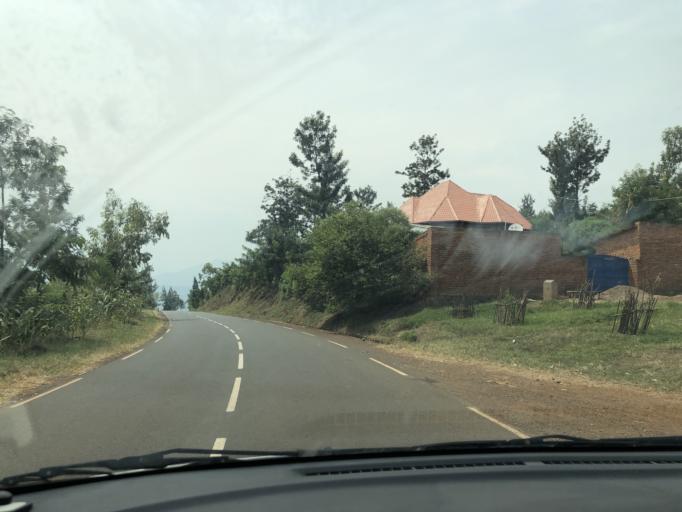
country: RW
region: Western Province
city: Cyangugu
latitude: -2.6694
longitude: 28.9960
